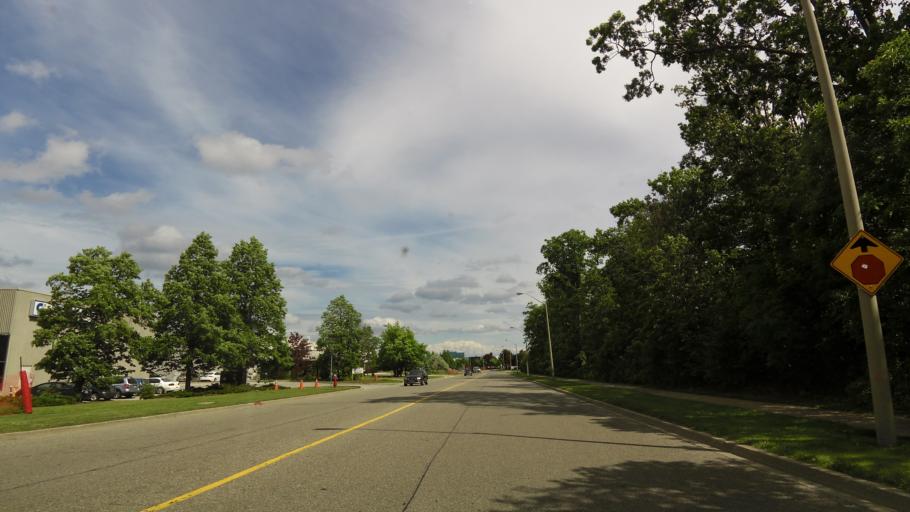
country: CA
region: Ontario
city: Oakville
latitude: 43.5114
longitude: -79.6769
